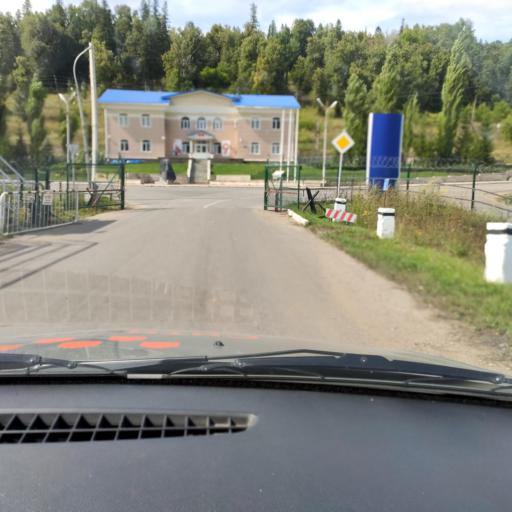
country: RU
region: Bashkortostan
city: Pavlovka
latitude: 55.4087
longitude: 56.5514
